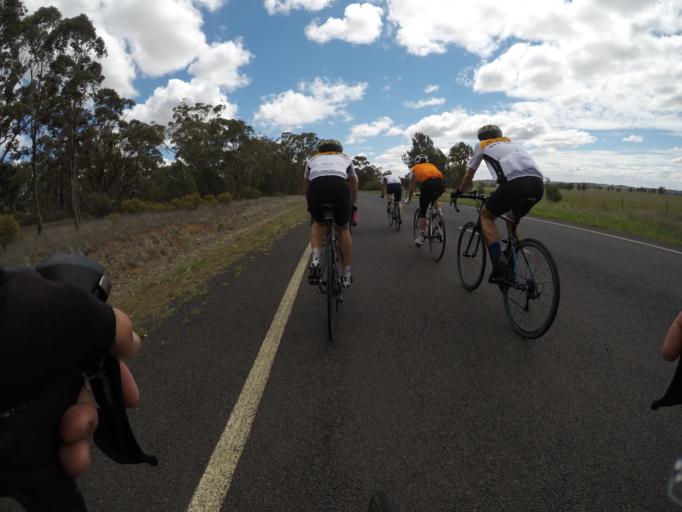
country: AU
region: New South Wales
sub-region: Dubbo Municipality
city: Dubbo
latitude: -32.4286
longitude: 148.5774
